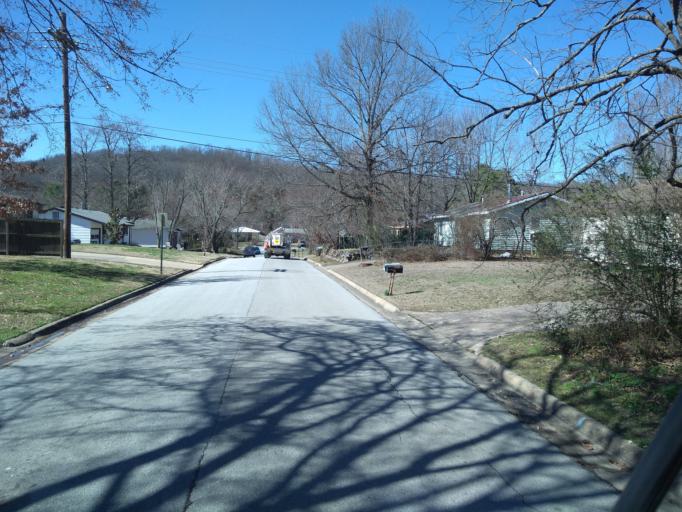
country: US
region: Arkansas
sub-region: Washington County
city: Fayetteville
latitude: 36.0430
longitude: -94.1877
